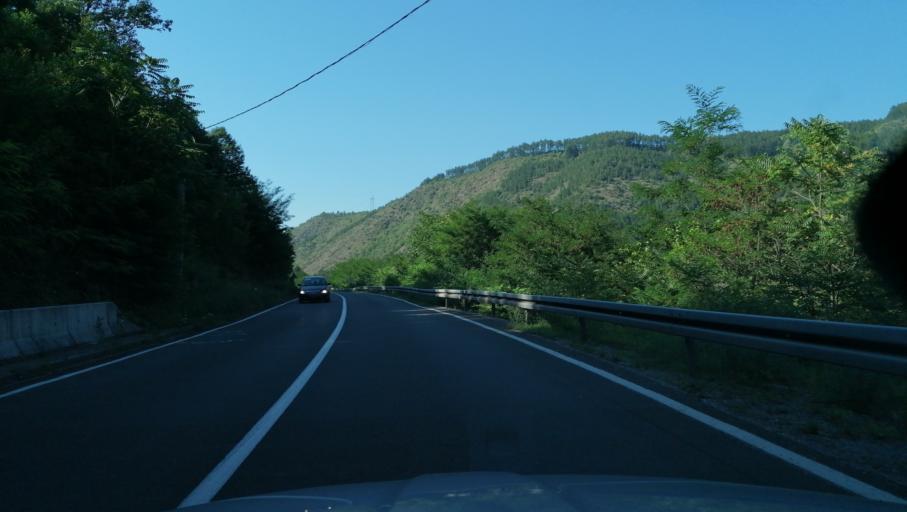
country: RS
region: Central Serbia
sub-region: Raski Okrug
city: Kraljevo
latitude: 43.6626
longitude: 20.5929
